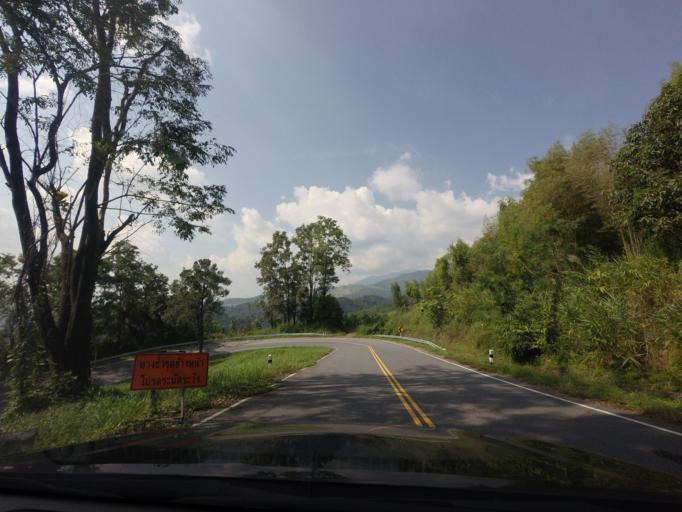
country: TH
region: Nan
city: Santi Suk
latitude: 18.9762
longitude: 100.9918
